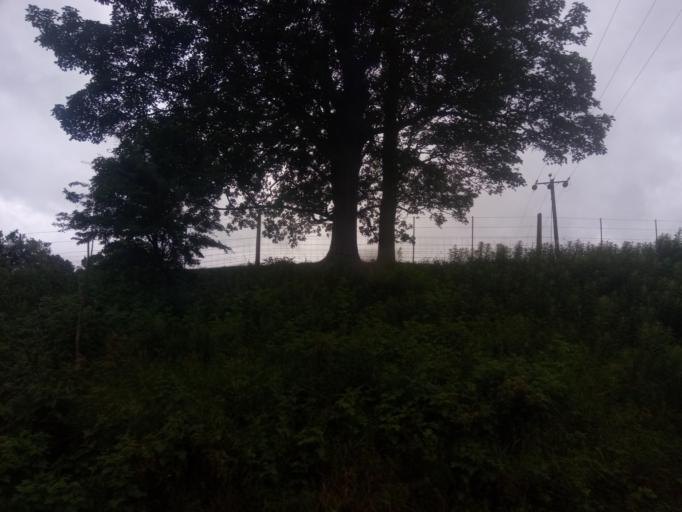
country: GB
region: England
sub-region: North Yorkshire
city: Settle
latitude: 54.0160
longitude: -2.2533
